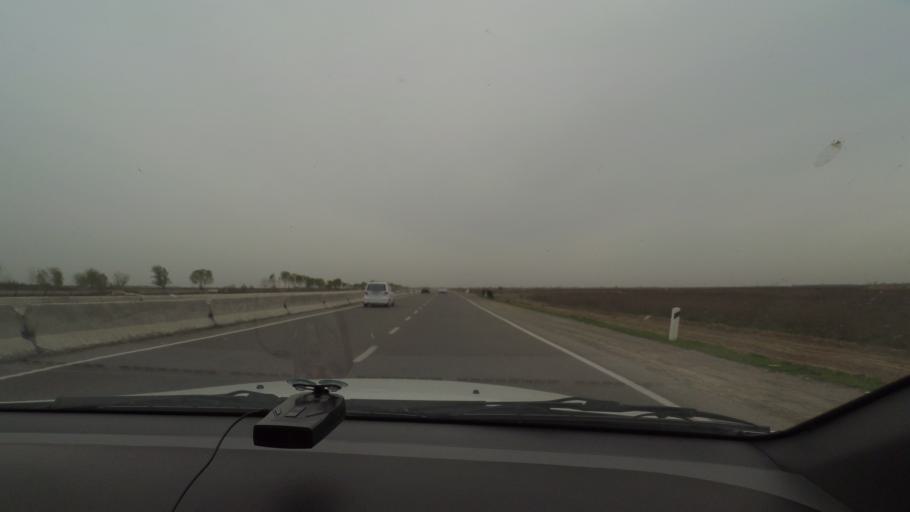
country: KZ
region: Ongtustik Qazaqstan
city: Myrzakent
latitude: 40.5152
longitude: 68.4823
